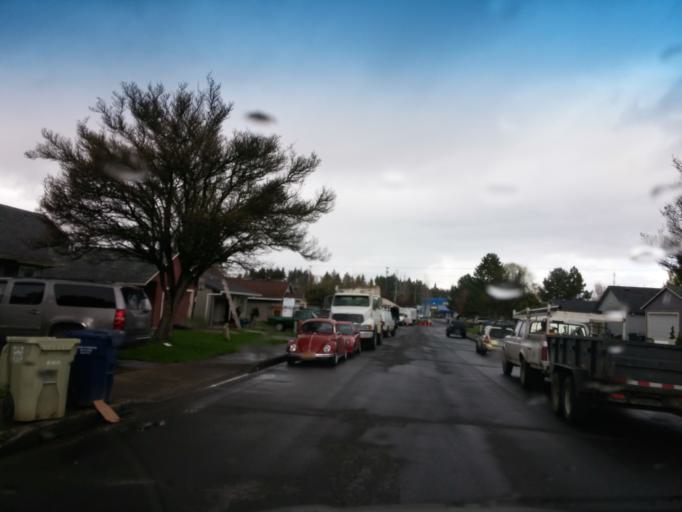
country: US
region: Oregon
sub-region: Washington County
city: Aloha
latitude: 45.5118
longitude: -122.8615
